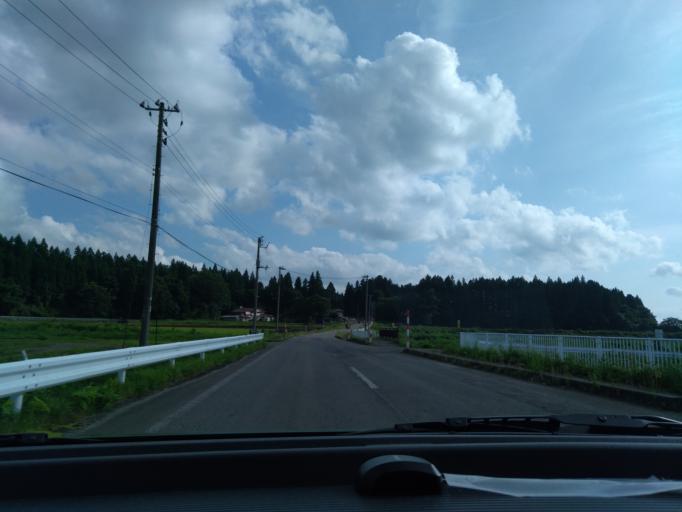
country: JP
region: Akita
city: Kakunodatemachi
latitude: 39.5934
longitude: 140.6142
